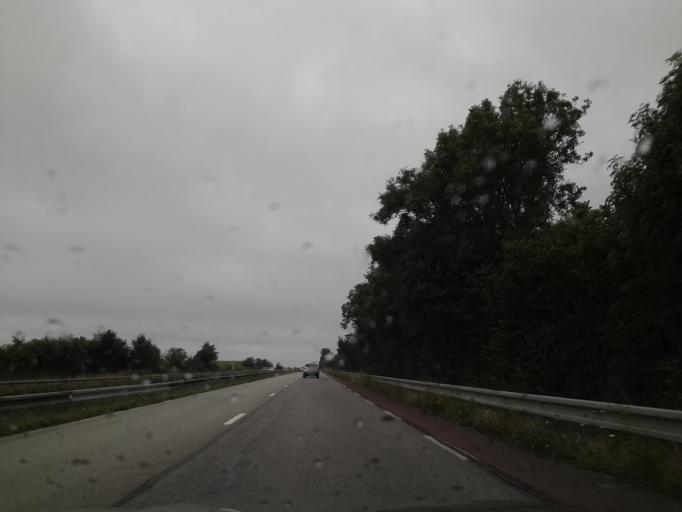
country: FR
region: Lower Normandy
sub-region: Departement de la Manche
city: Sainte-Mere-Eglise
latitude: 49.4400
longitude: -1.3418
